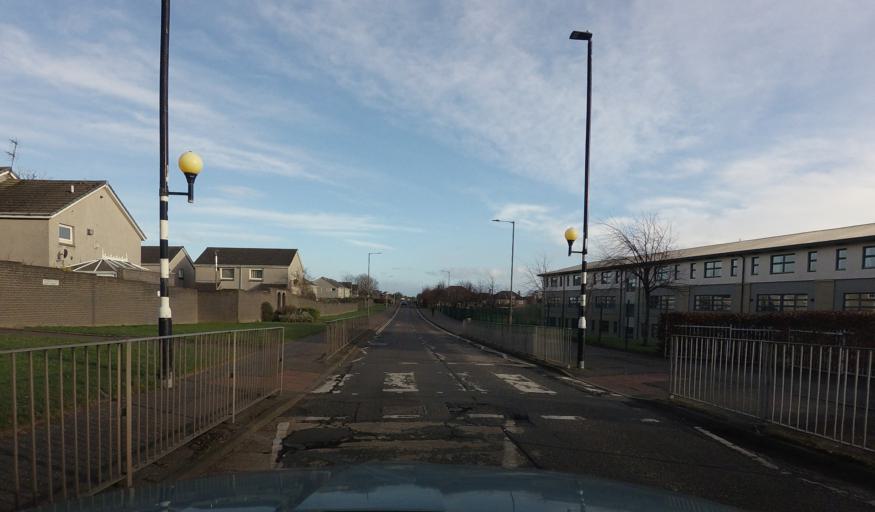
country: GB
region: Scotland
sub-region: Edinburgh
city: Currie
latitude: 55.9457
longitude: -3.3045
